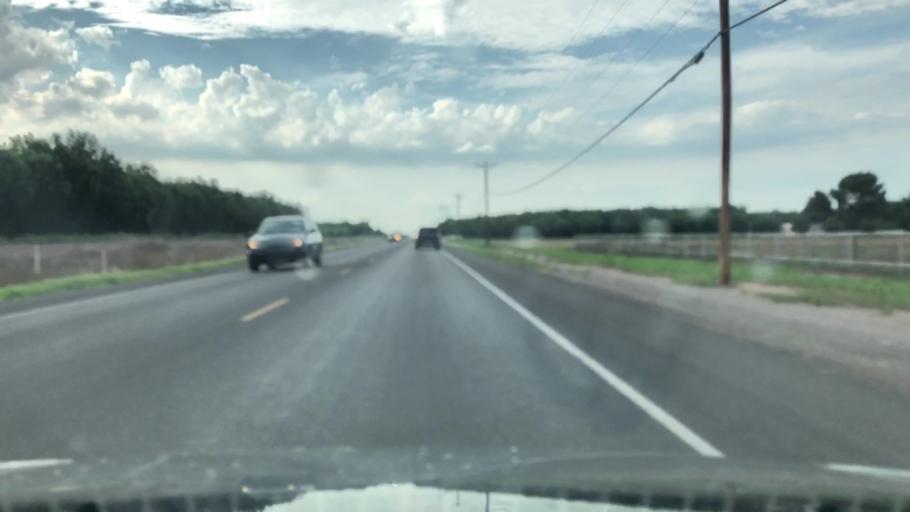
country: US
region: New Mexico
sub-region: Dona Ana County
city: San Miguel
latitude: 32.2183
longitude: -106.7304
